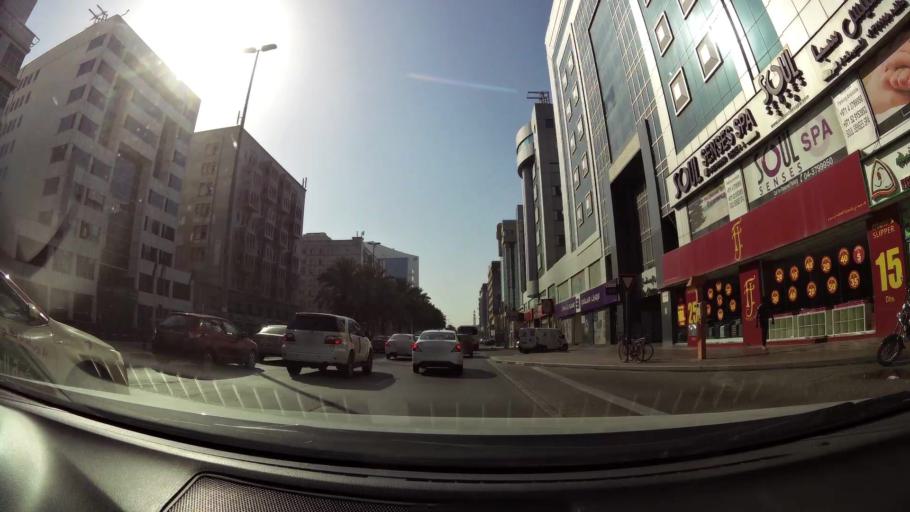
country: AE
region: Ash Shariqah
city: Sharjah
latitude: 25.2573
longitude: 55.2990
